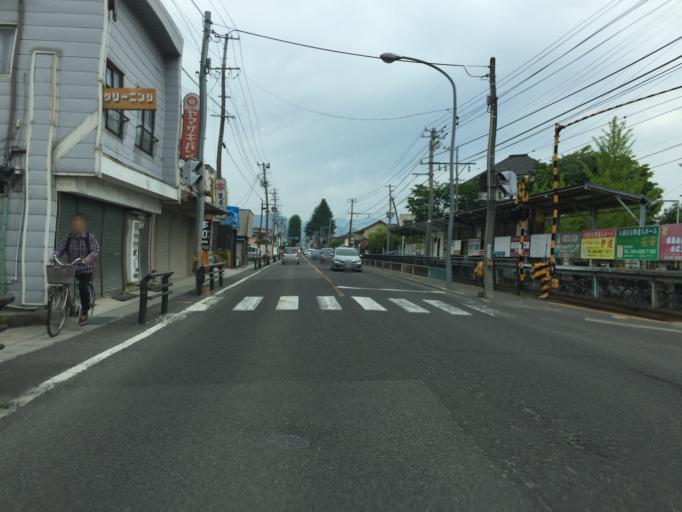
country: JP
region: Fukushima
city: Fukushima-shi
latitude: 37.7831
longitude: 140.4412
